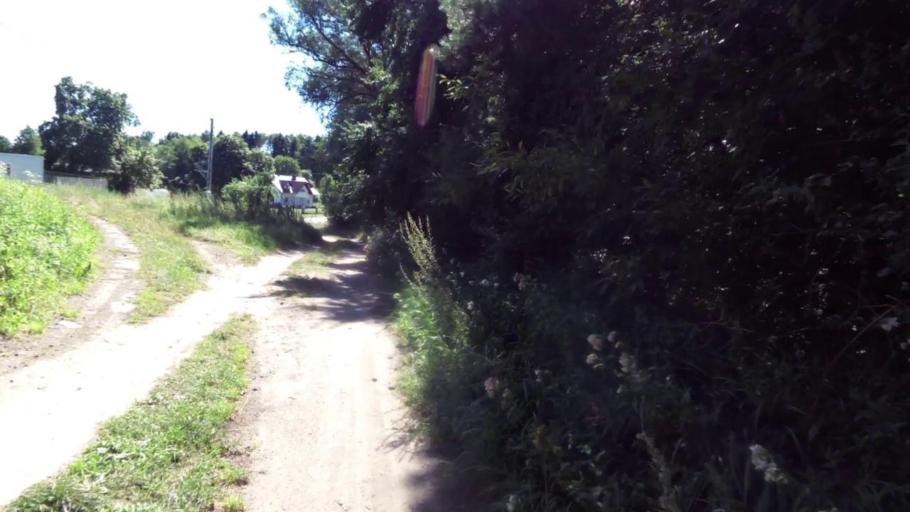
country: PL
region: West Pomeranian Voivodeship
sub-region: Powiat szczecinecki
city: Bialy Bor
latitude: 53.8351
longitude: 16.8737
